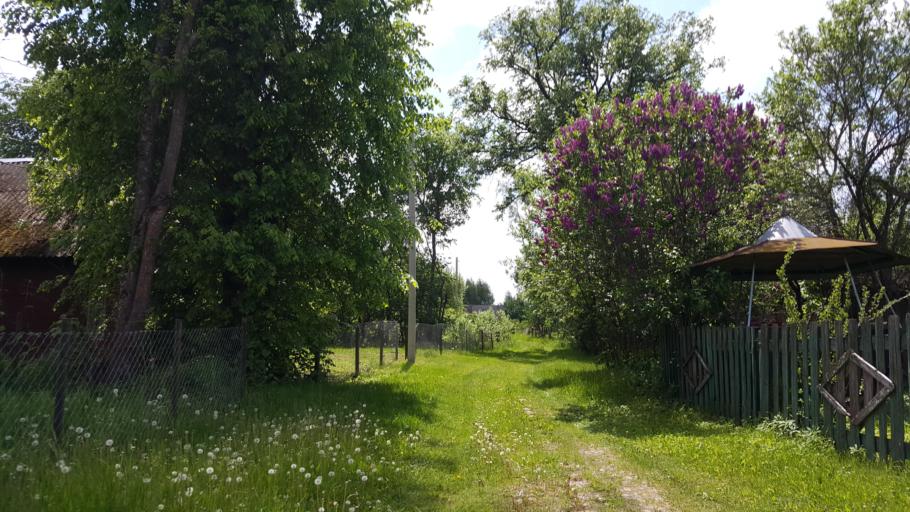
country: BY
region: Brest
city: Kamyanyets
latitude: 52.4779
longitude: 23.9721
